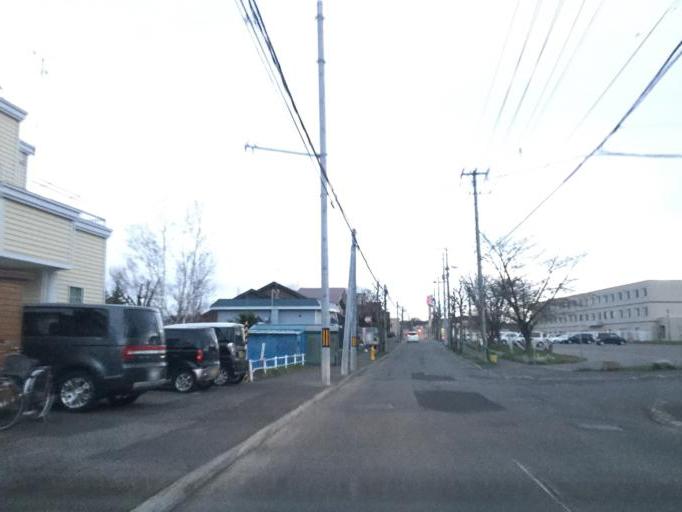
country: JP
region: Hokkaido
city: Sapporo
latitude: 43.0189
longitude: 141.4254
